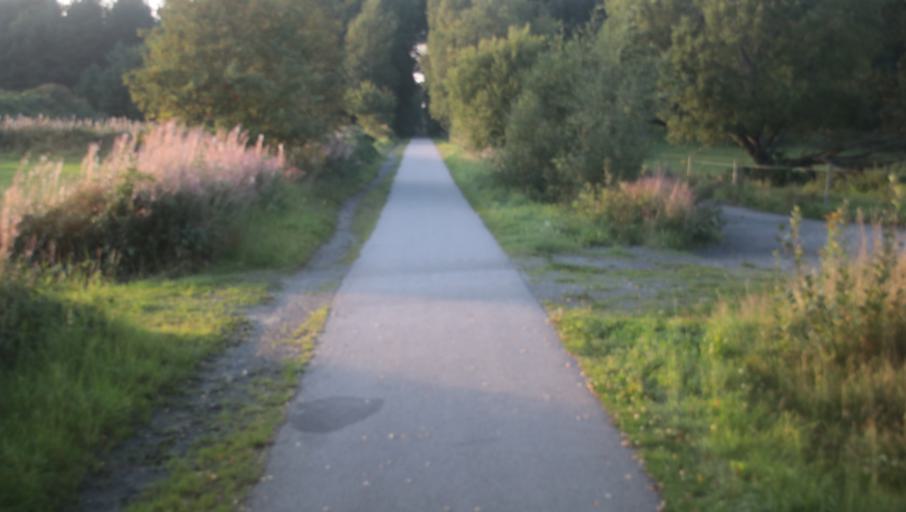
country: SE
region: Blekinge
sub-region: Karlshamns Kommun
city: Karlshamn
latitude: 56.2181
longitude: 14.8226
